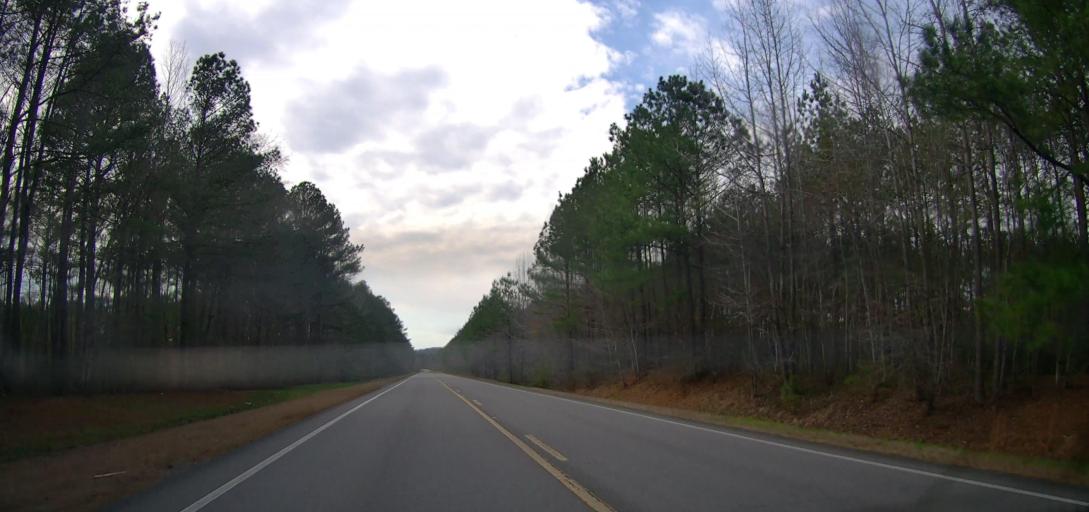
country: US
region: Alabama
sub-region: Marion County
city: Winfield
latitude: 33.9340
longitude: -87.7111
